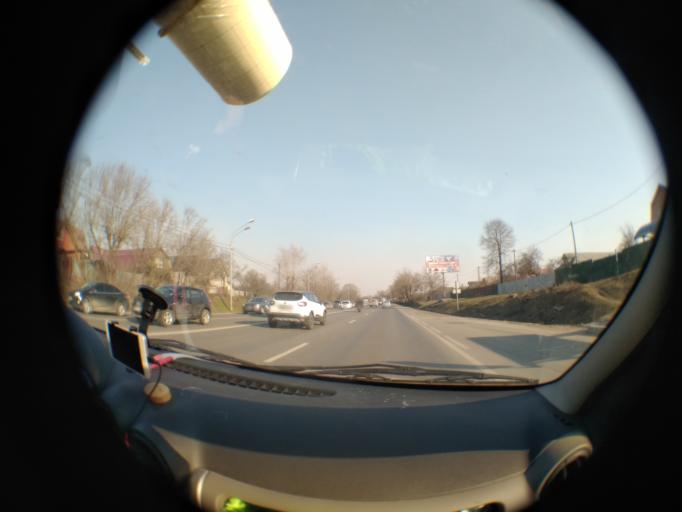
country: RU
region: Moskovskaya
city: Ostrovtsy
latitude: 55.5938
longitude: 37.9958
